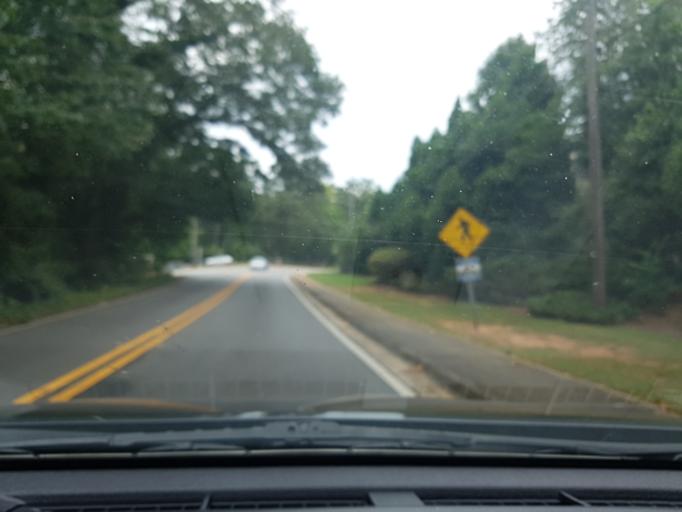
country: US
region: Georgia
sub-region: Clayton County
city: Morrow
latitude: 33.5916
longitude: -84.3514
